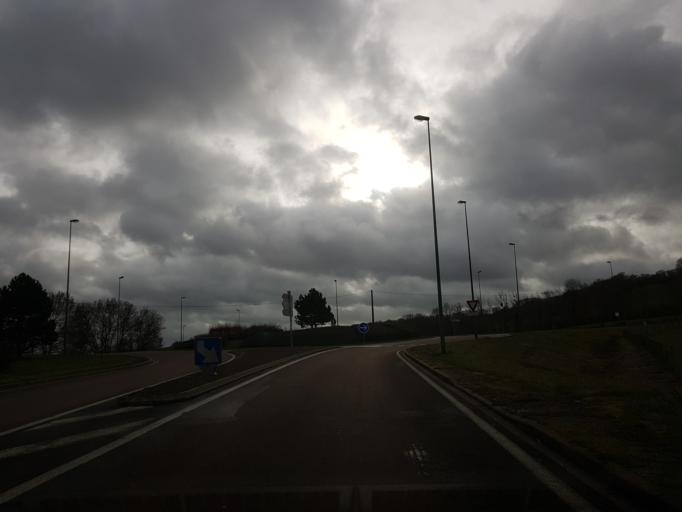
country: FR
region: Champagne-Ardenne
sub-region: Departement de la Haute-Marne
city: Langres
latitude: 47.8549
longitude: 5.3454
